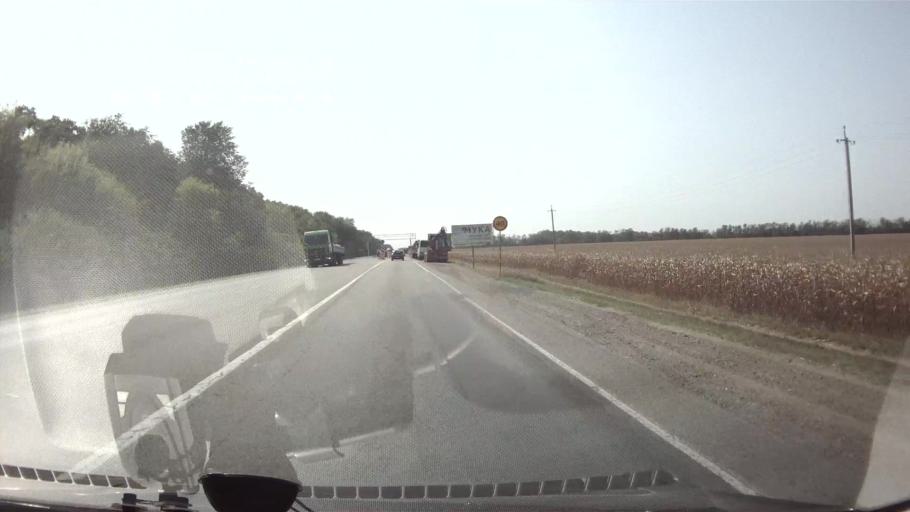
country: RU
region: Krasnodarskiy
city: Vasyurinskaya
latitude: 45.1555
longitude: 39.4515
